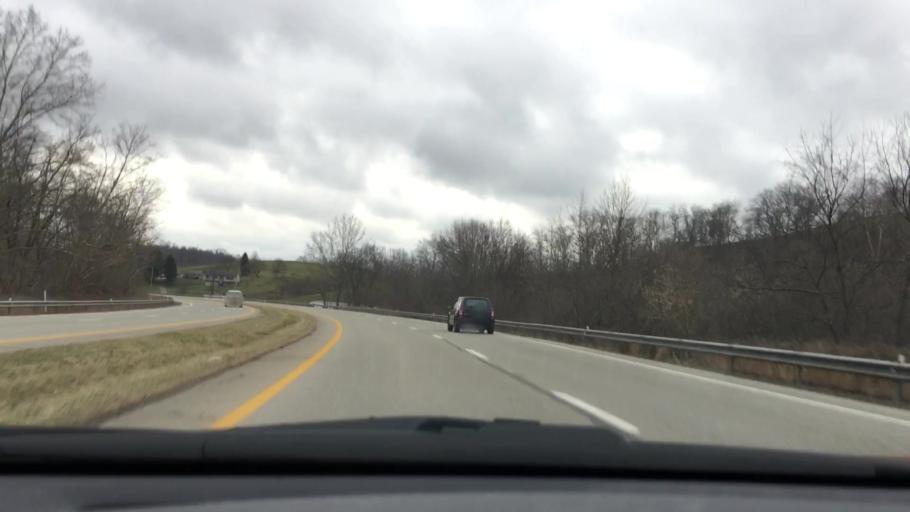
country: US
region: Pennsylvania
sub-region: Fayette County
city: Oliver
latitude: 39.9541
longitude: -79.7434
